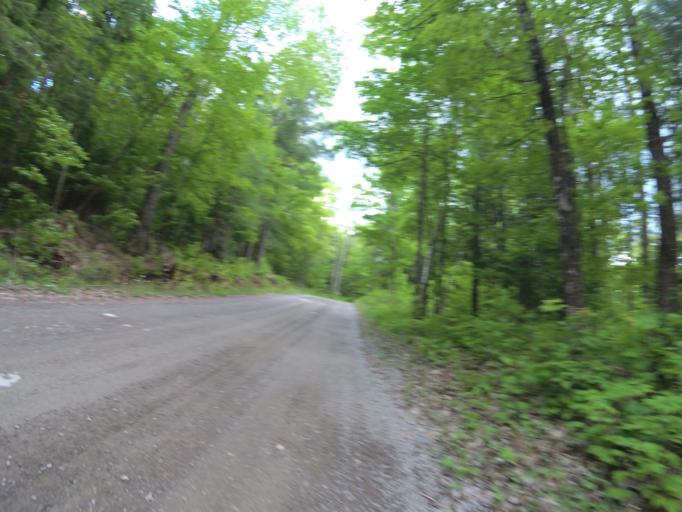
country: CA
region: Ontario
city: Renfrew
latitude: 45.1914
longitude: -76.9052
